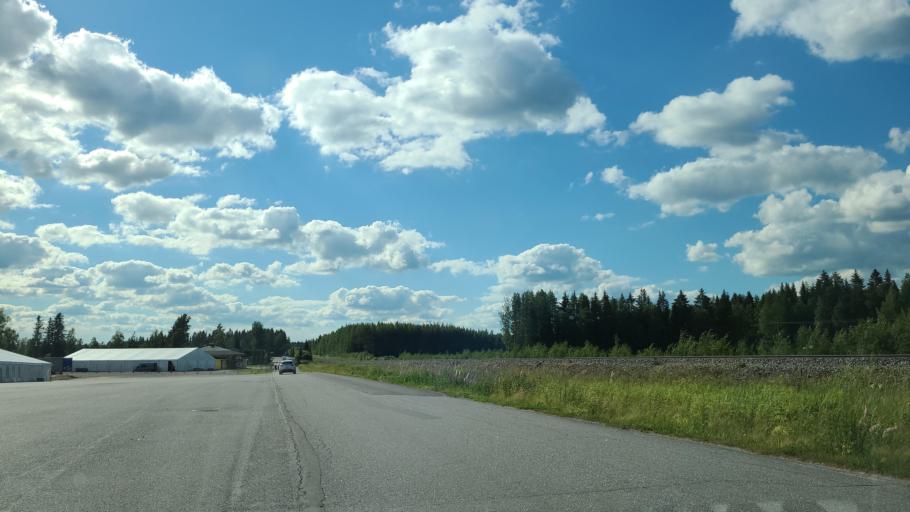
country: FI
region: Southern Ostrobothnia
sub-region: Kuusiokunnat
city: Toeysae
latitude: 62.6053
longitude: 23.7209
